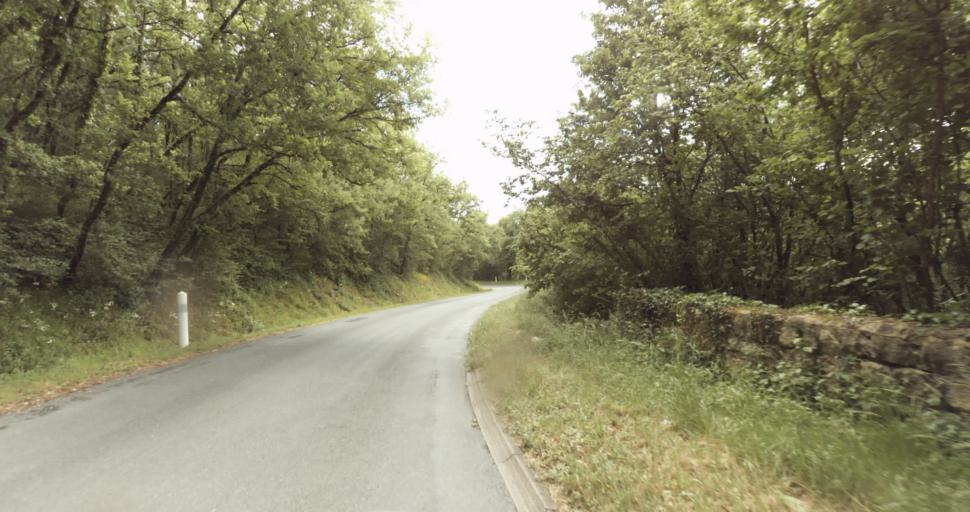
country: FR
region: Aquitaine
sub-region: Departement de la Dordogne
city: Beaumont-du-Perigord
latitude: 44.7579
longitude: 0.7292
